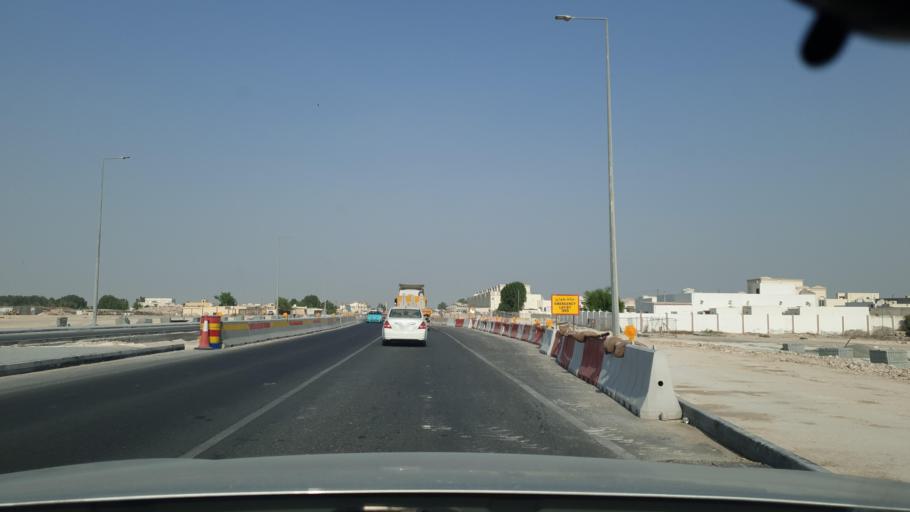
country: QA
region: Al Wakrah
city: Al Wukayr
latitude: 25.1468
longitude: 51.5208
